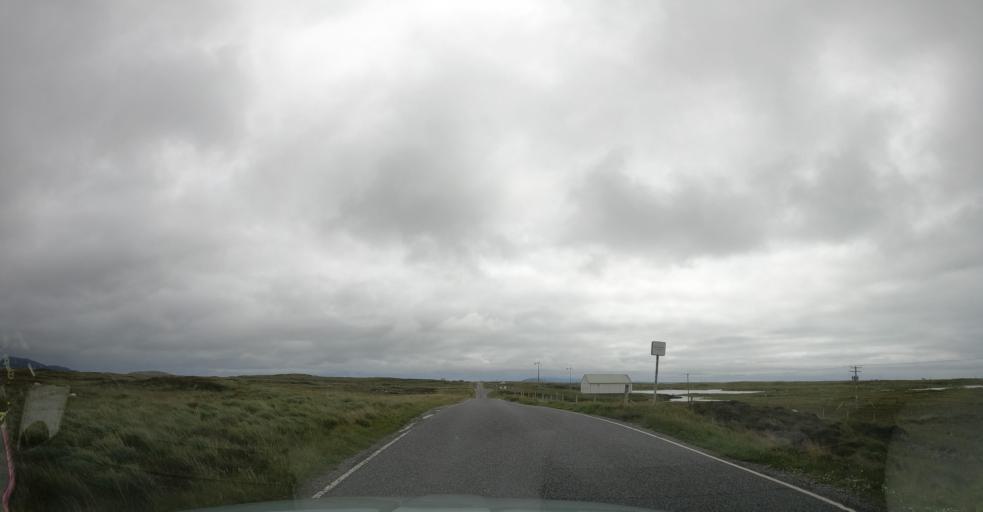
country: GB
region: Scotland
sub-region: Eilean Siar
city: Isle of North Uist
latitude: 57.5472
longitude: -7.3273
